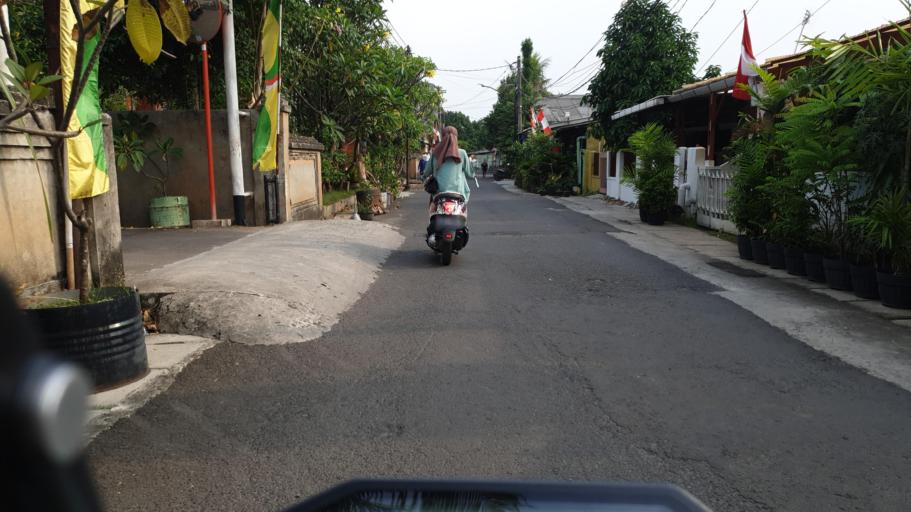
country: ID
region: West Java
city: Depok
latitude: -6.3402
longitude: 106.8312
